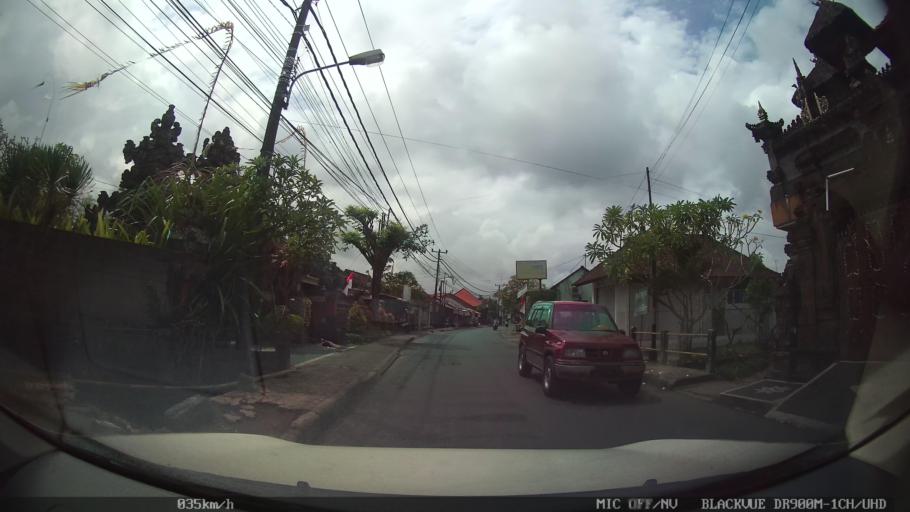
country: ID
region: Bali
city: Banjar Bucu
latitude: -8.5829
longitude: 115.1906
